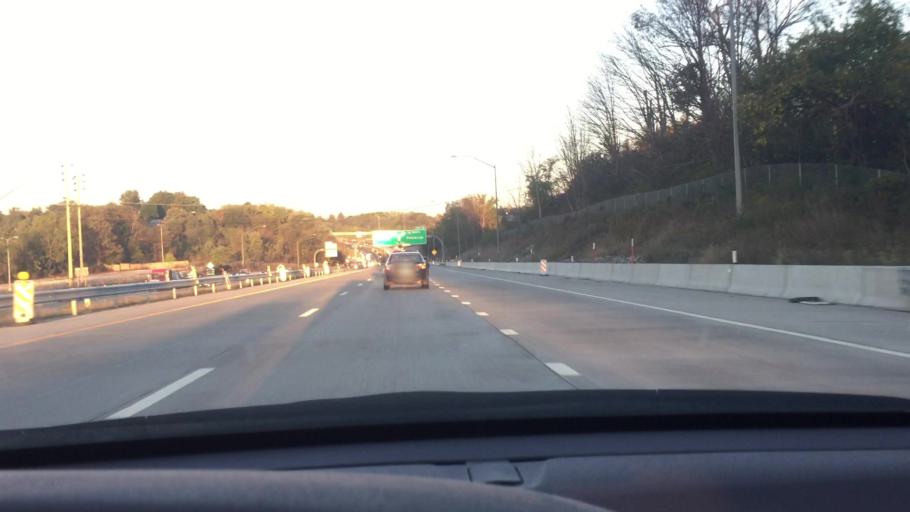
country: US
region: Pennsylvania
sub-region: Washington County
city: East Washington
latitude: 40.1867
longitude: -80.2354
